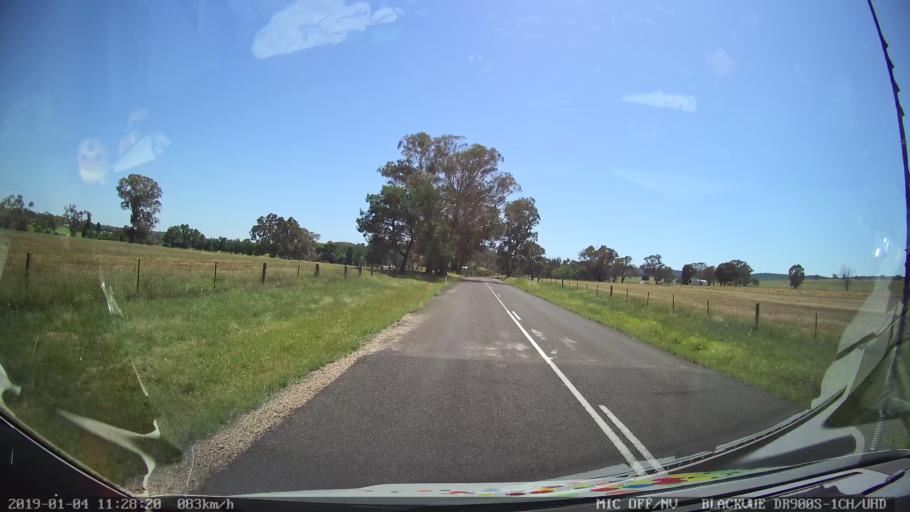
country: AU
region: New South Wales
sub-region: Cabonne
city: Molong
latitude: -33.1006
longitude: 148.7711
